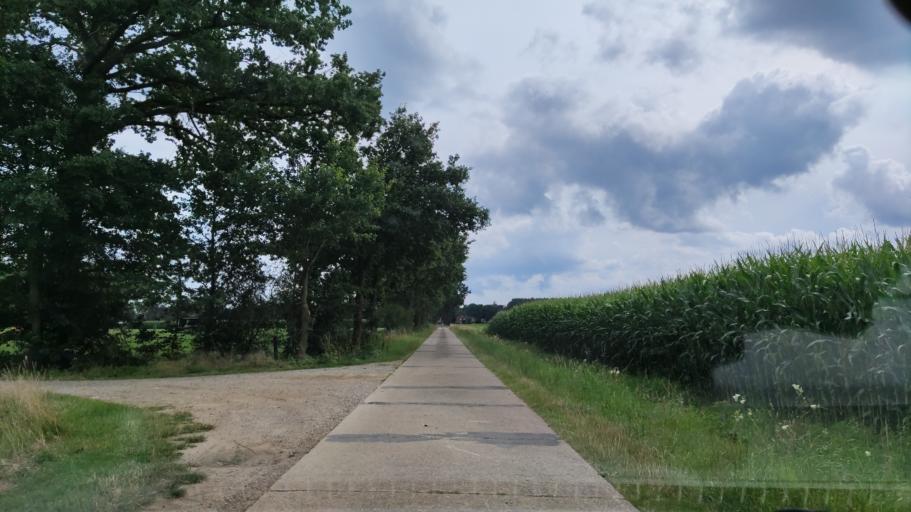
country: DE
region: Lower Saxony
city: Damnatz
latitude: 53.1024
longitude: 11.1447
